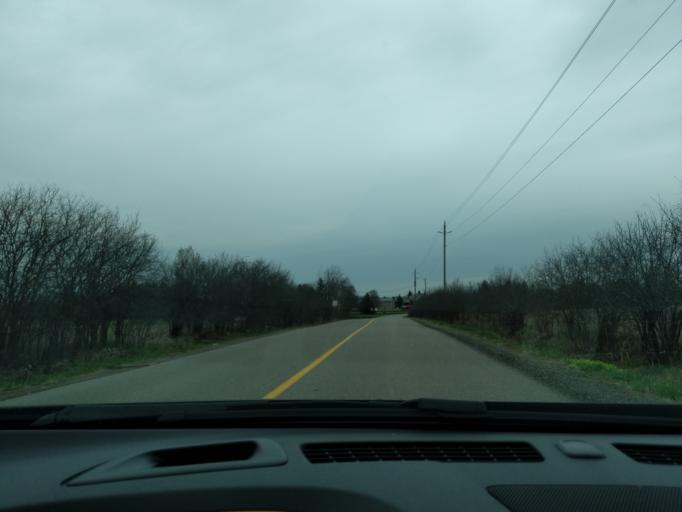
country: CA
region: Ontario
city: Brampton
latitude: 43.8050
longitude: -79.7956
